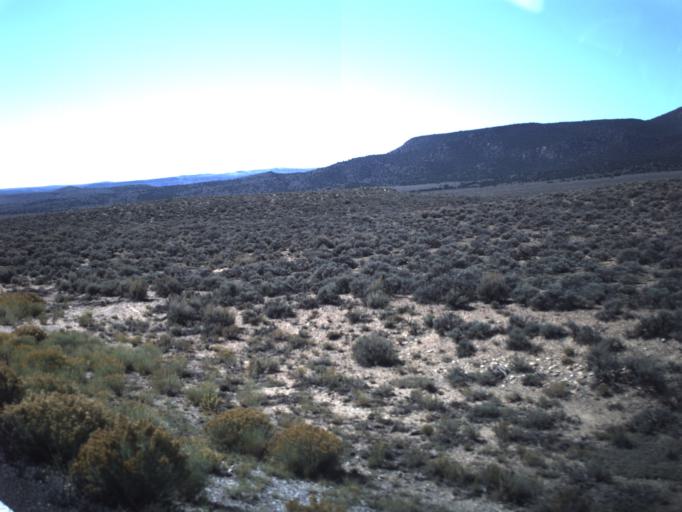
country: US
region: Utah
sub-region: Piute County
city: Junction
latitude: 38.2221
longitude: -111.9991
